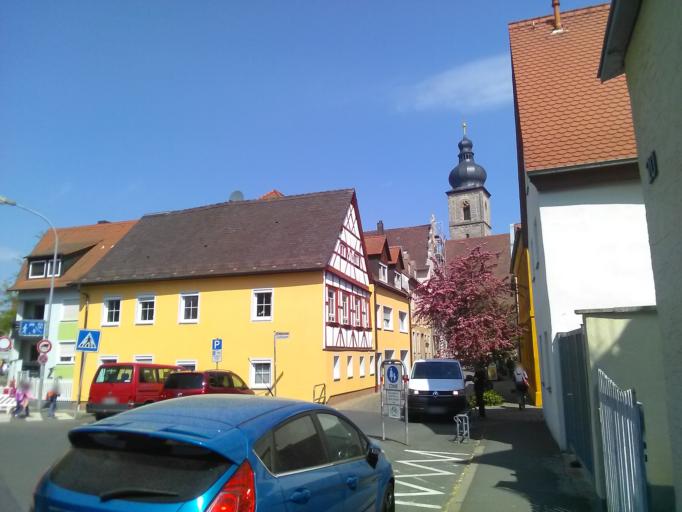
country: DE
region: Bavaria
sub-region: Upper Franconia
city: Forchheim
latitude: 49.7187
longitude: 11.0574
